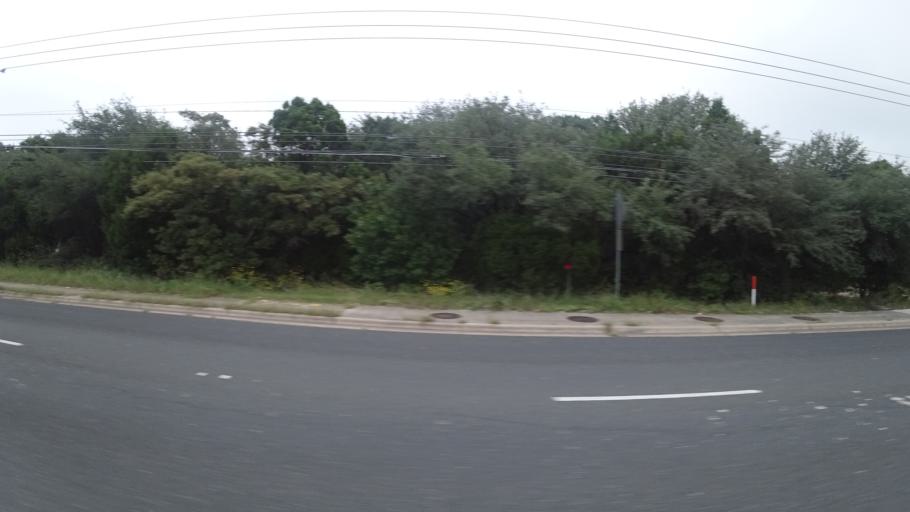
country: US
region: Texas
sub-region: Travis County
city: Wells Branch
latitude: 30.3660
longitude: -97.6687
